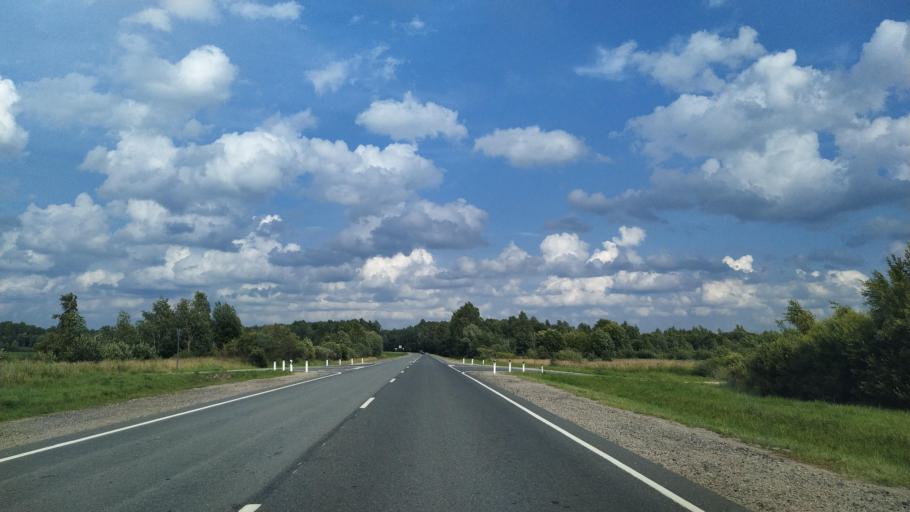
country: RU
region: Novgorod
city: Sol'tsy
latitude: 58.1372
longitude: 30.4011
